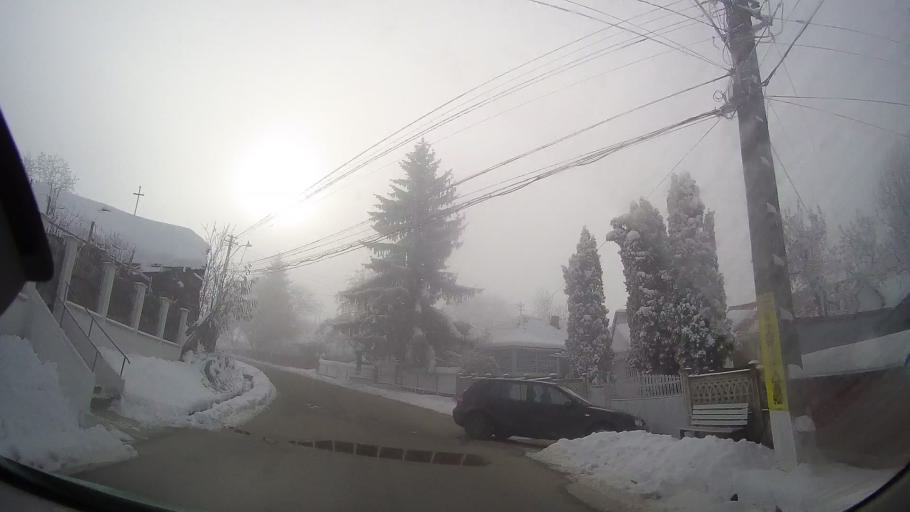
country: RO
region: Iasi
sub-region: Comuna Valea Seaca
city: Topile
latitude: 47.2599
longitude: 26.6668
